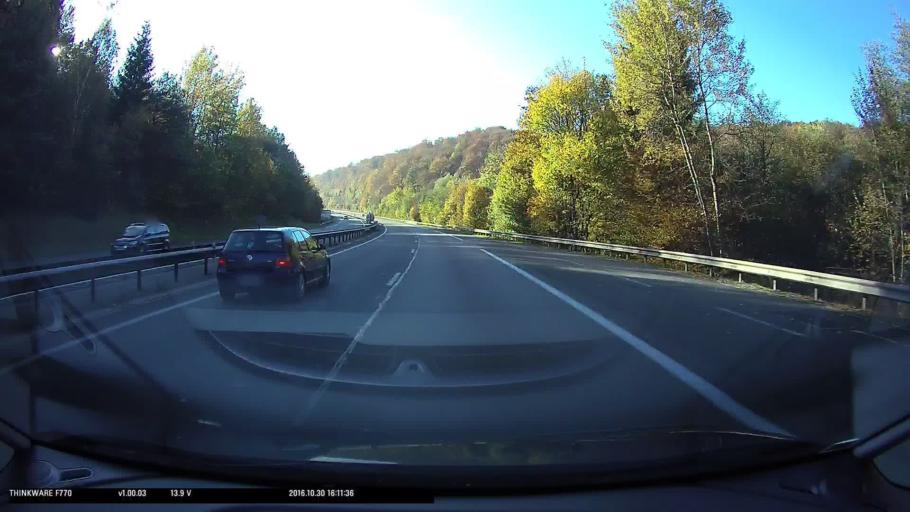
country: FR
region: Franche-Comte
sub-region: Departement du Doubs
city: Colombier-Fontaine
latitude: 47.4289
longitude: 6.6612
